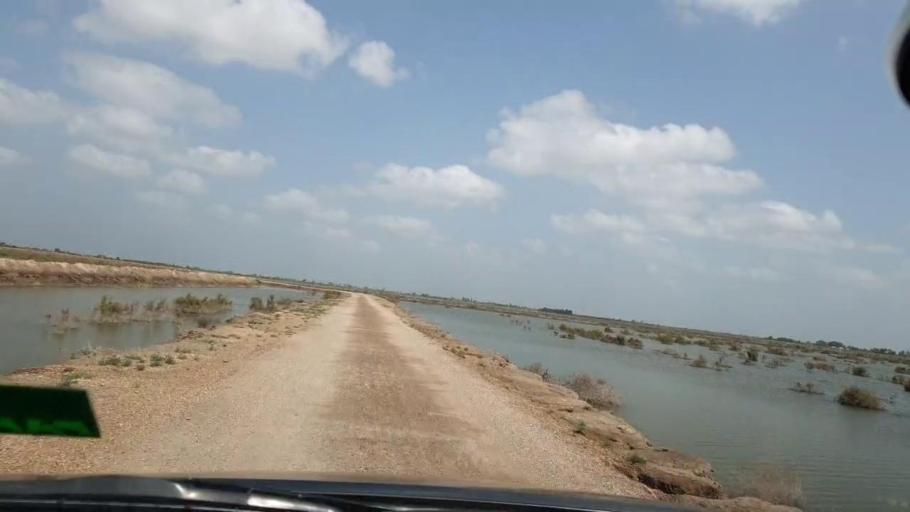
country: PK
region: Sindh
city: Kadhan
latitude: 24.5848
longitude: 69.1395
